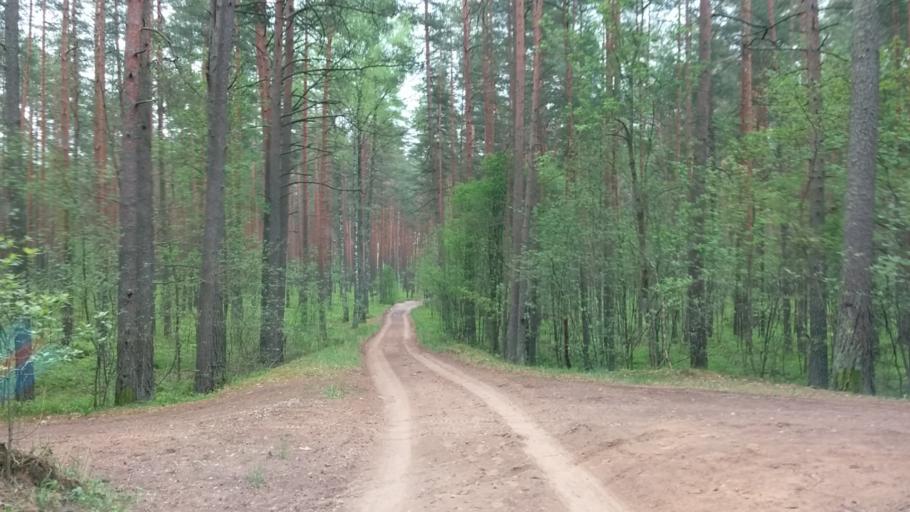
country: LV
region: Babite
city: Pinki
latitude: 56.9362
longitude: 23.9285
